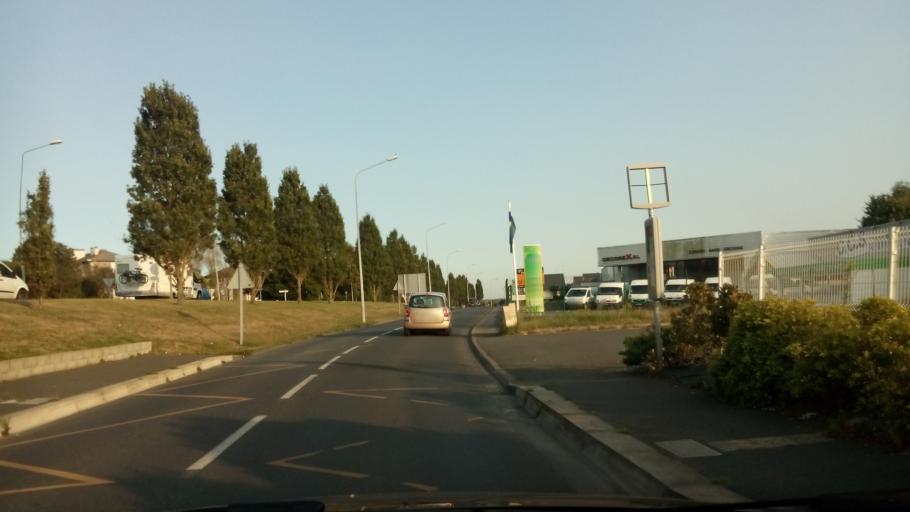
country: FR
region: Brittany
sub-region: Departement des Cotes-d'Armor
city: Lannion
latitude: 48.7445
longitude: -3.4761
